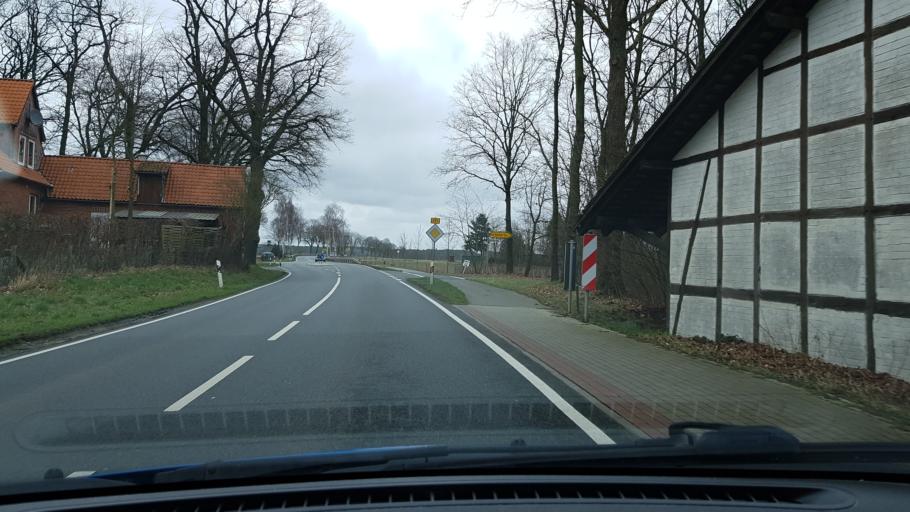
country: DE
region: Lower Saxony
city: Stoetze
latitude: 53.0541
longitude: 10.8202
